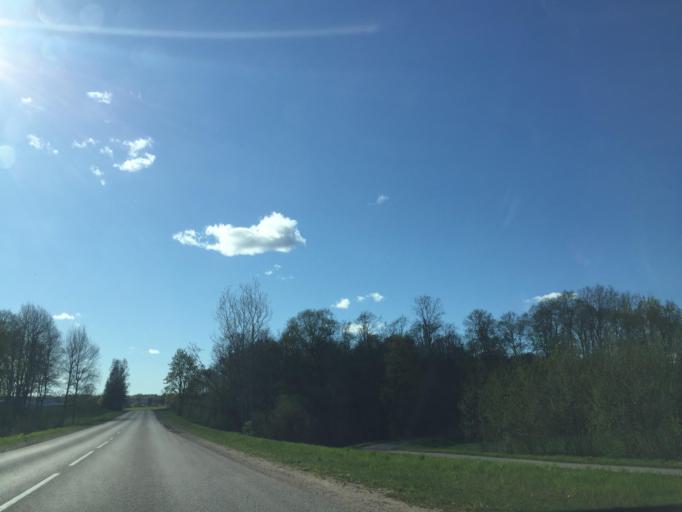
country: LV
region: Madonas Rajons
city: Madona
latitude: 56.8066
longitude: 26.0312
